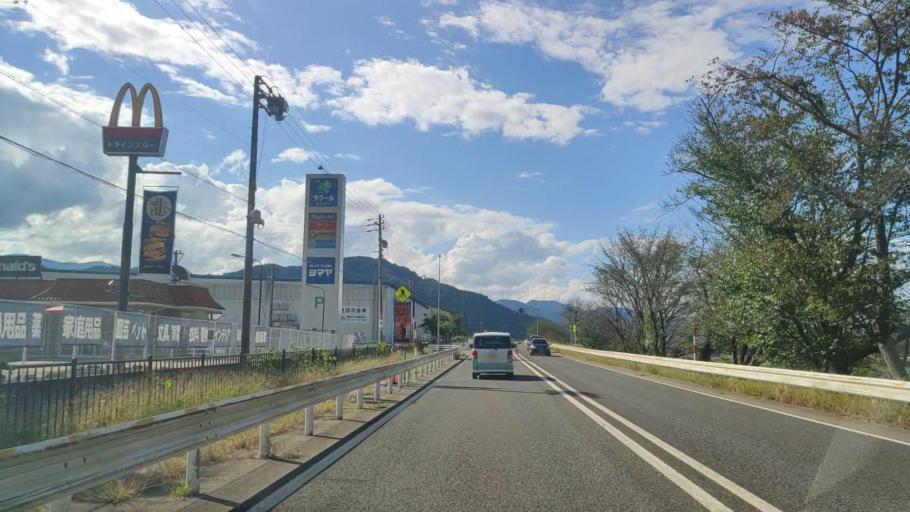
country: JP
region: Gifu
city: Takayama
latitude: 36.2057
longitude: 137.2227
